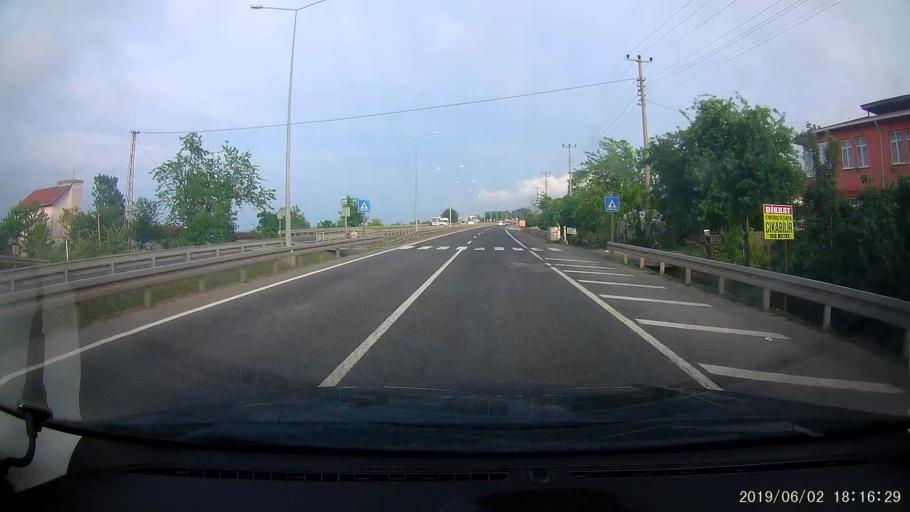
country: TR
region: Ordu
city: Unieh
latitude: 41.0998
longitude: 37.3996
